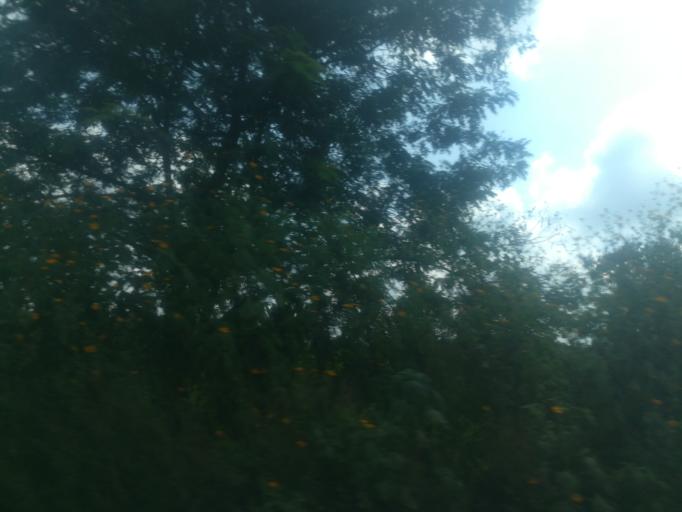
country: NG
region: Oyo
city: Moniya
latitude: 7.5785
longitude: 3.9151
